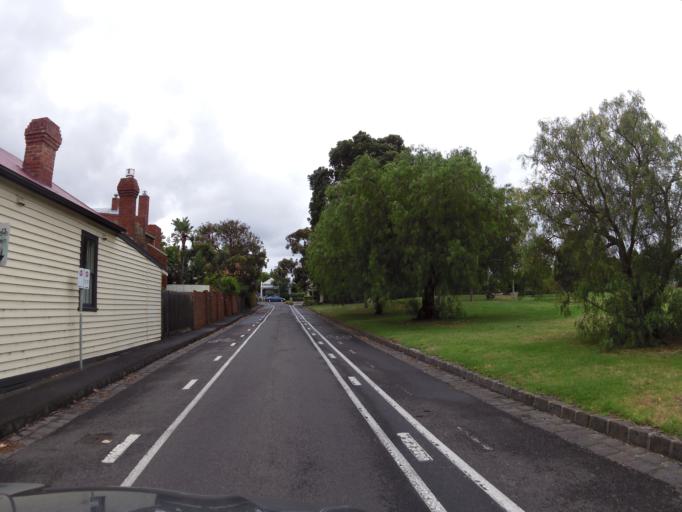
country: AU
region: Victoria
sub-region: Yarra
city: Clifton Hill
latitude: -37.7905
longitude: 145.0007
